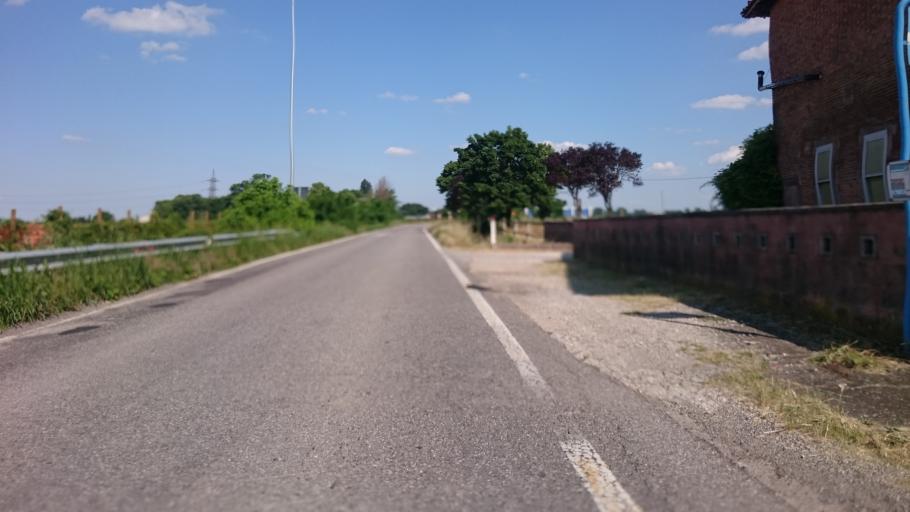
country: IT
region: Lombardy
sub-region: Provincia di Mantova
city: Mottella
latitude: 45.1542
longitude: 10.8572
